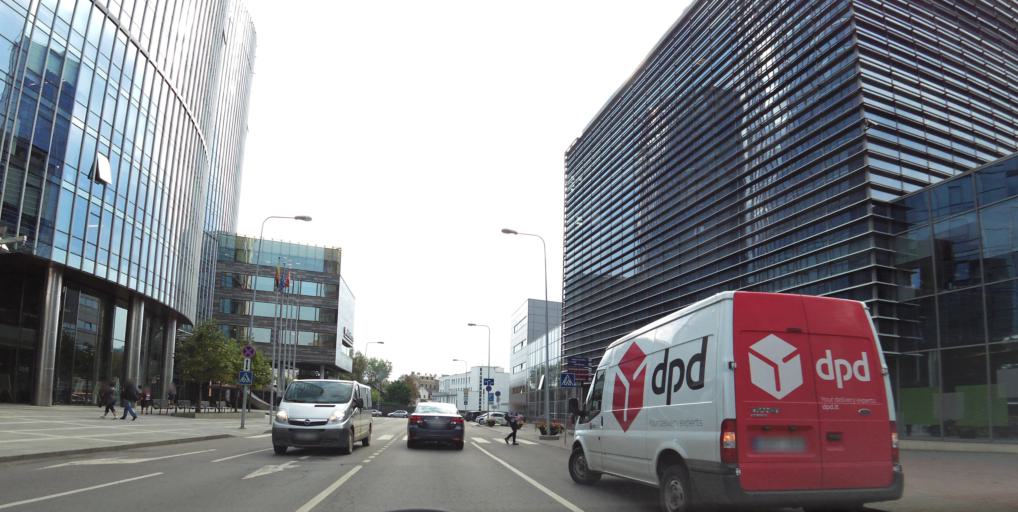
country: LT
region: Vilnius County
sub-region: Vilnius
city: Vilnius
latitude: 54.6966
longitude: 25.2784
